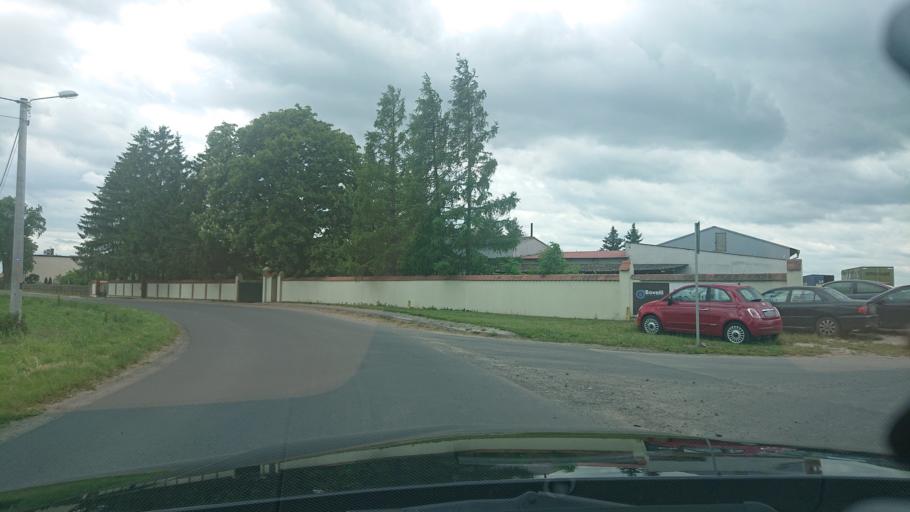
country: PL
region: Greater Poland Voivodeship
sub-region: Powiat gnieznienski
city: Gniezno
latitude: 52.5416
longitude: 17.5384
